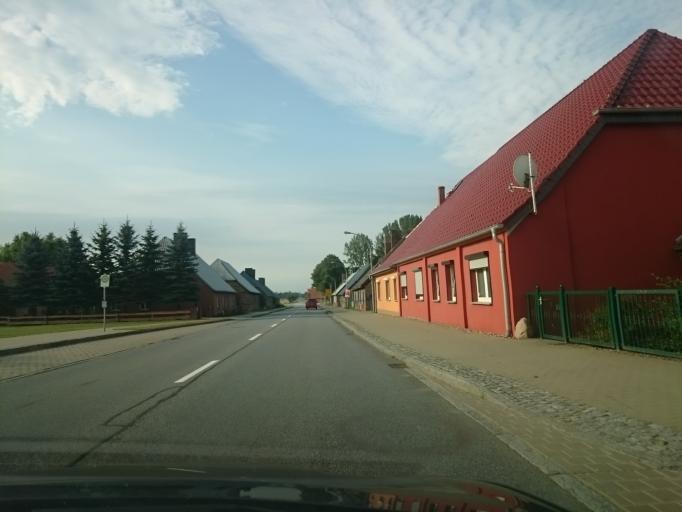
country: DE
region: Mecklenburg-Vorpommern
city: Wackerow
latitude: 53.7242
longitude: 12.9185
